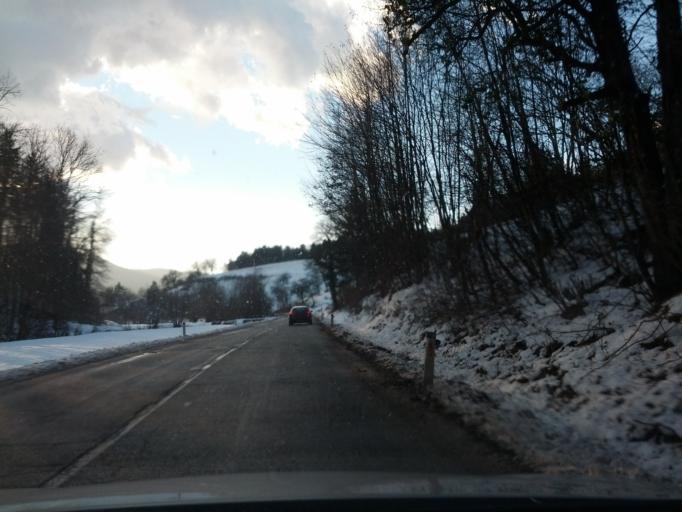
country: SI
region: Moravce
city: Moravce
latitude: 46.1330
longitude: 14.7736
